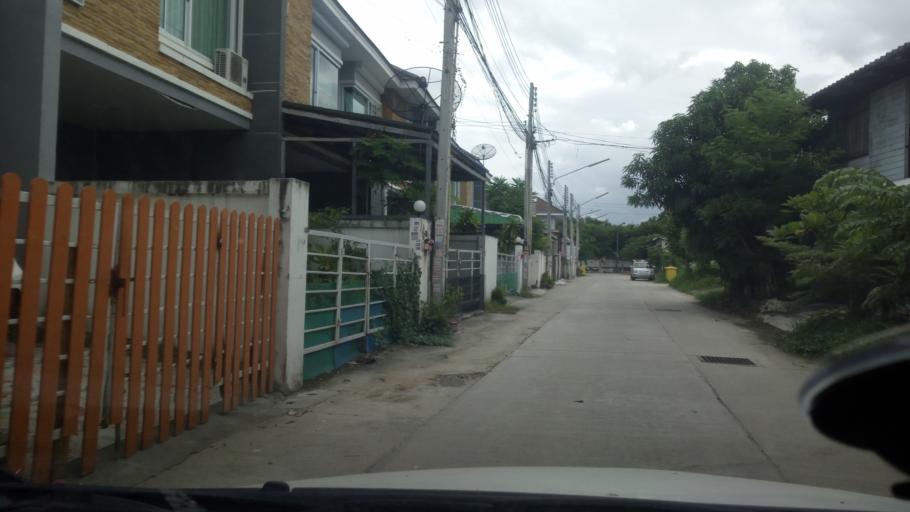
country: TH
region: Chon Buri
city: Phan Thong
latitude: 13.4116
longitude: 101.0522
